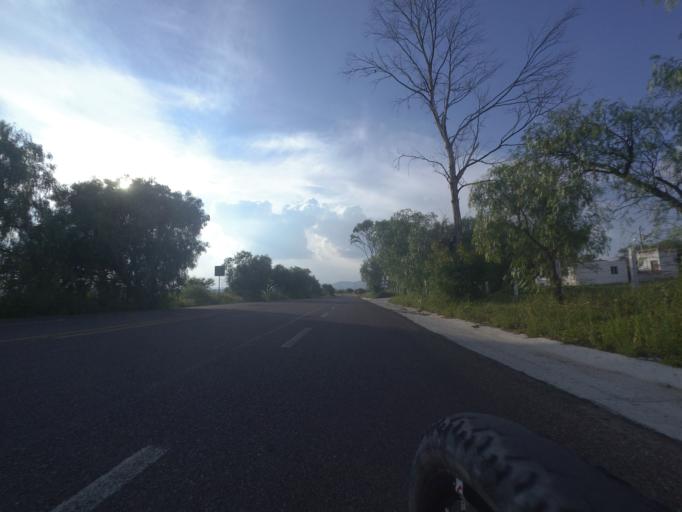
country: MX
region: Aguascalientes
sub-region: Aguascalientes
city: Penuelas (El Cienegal)
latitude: 21.7649
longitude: -102.3532
